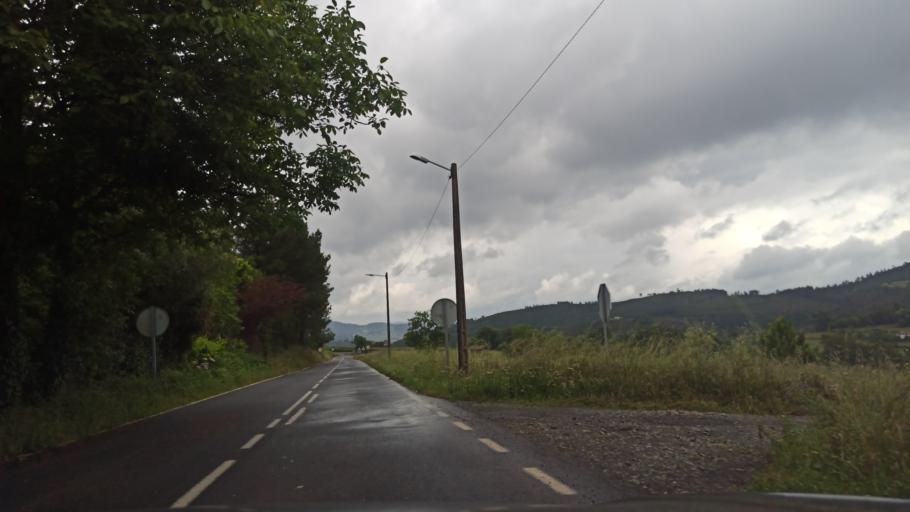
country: ES
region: Galicia
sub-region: Provincia da Coruna
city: Santiso
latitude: 42.7876
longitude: -8.0818
